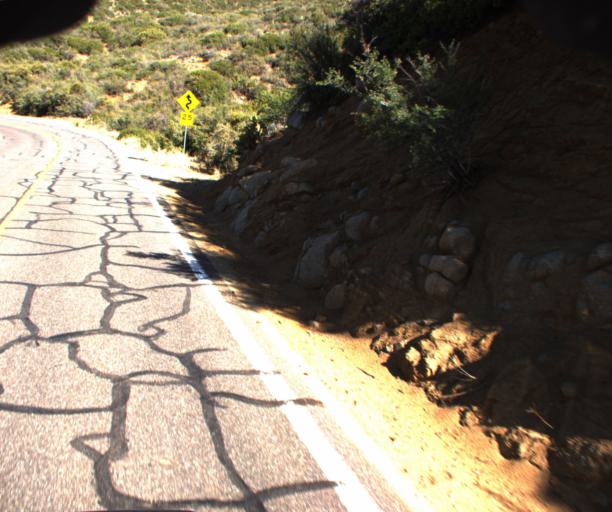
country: US
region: Arizona
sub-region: Yavapai County
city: Prescott
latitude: 34.4288
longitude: -112.5514
